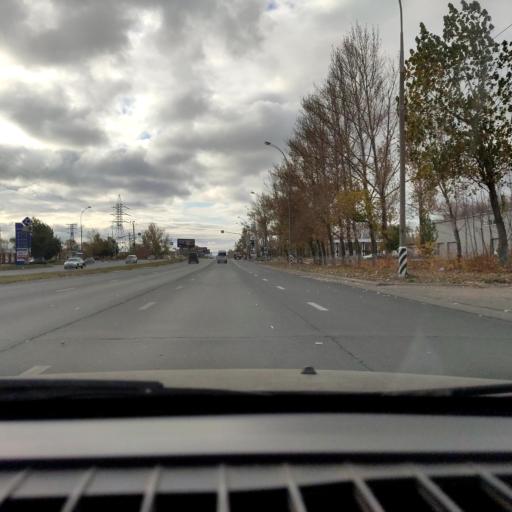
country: RU
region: Samara
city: Tol'yatti
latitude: 53.5476
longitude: 49.2860
